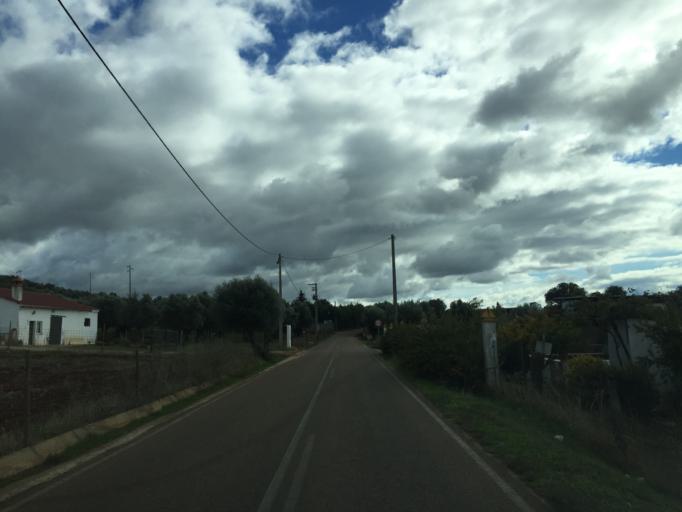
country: PT
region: Portalegre
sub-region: Alter do Chao
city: Alter do Chao
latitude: 39.2101
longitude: -7.6664
